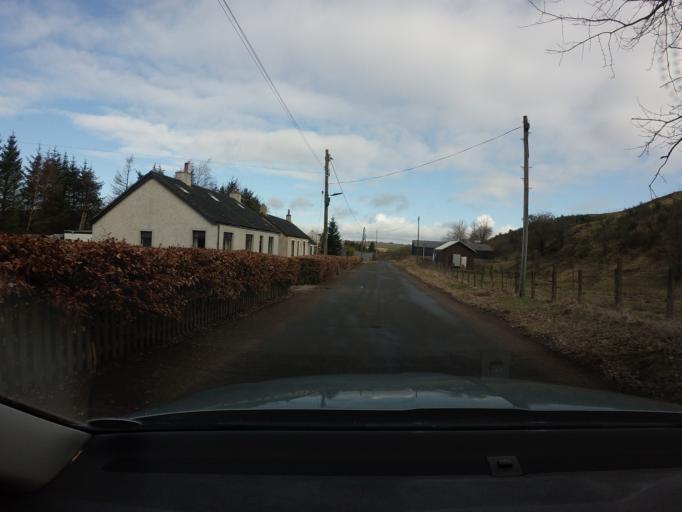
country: GB
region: Scotland
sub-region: South Lanarkshire
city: Lanark
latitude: 55.6052
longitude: -3.7879
